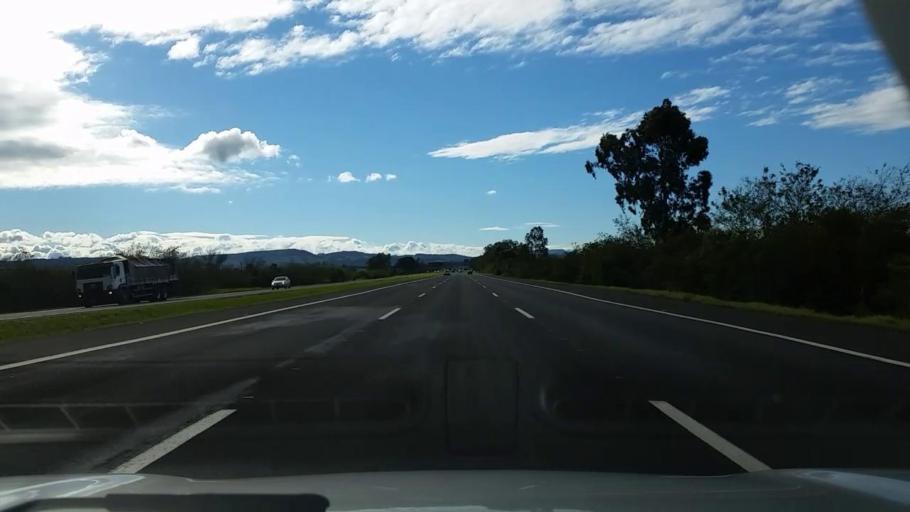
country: BR
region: Rio Grande do Sul
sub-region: Rolante
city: Rolante
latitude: -29.8819
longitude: -50.5267
